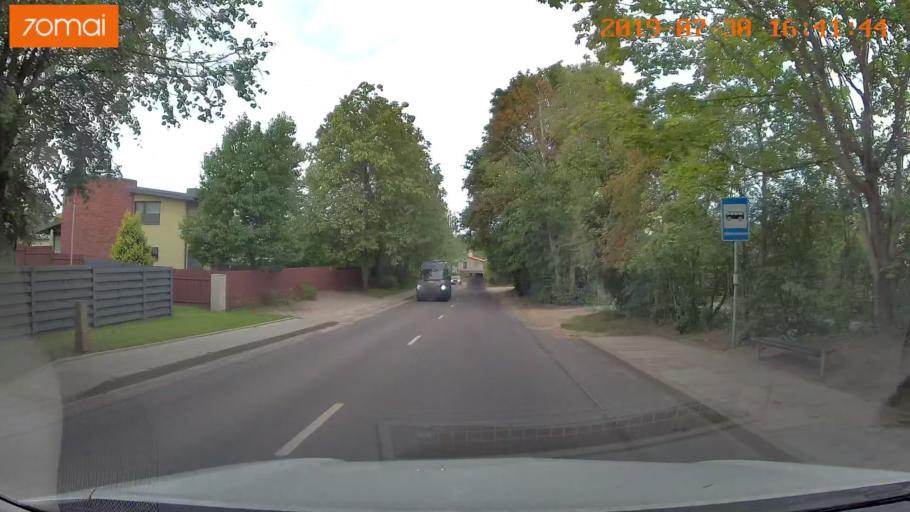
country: LT
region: Vilnius County
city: Rasos
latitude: 54.7133
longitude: 25.3525
